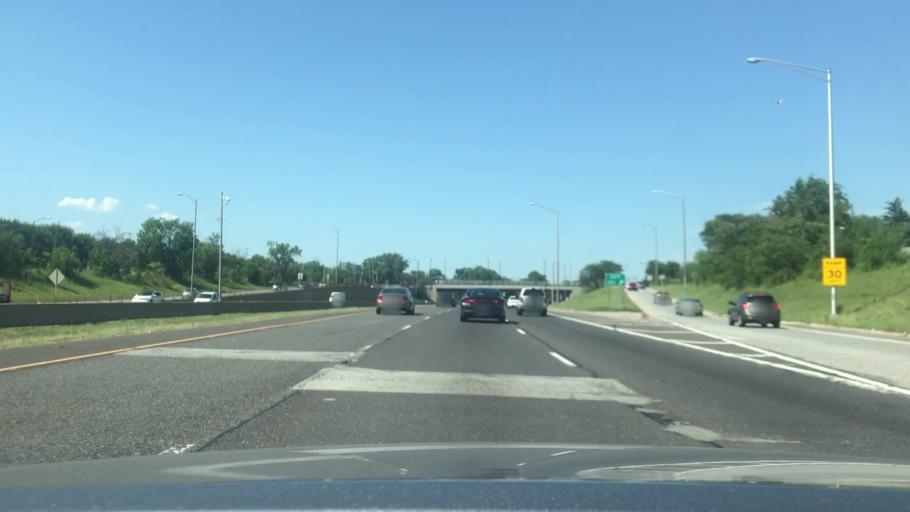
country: US
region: Illinois
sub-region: Cook County
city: Calumet Park
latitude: 41.6862
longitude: -87.6619
